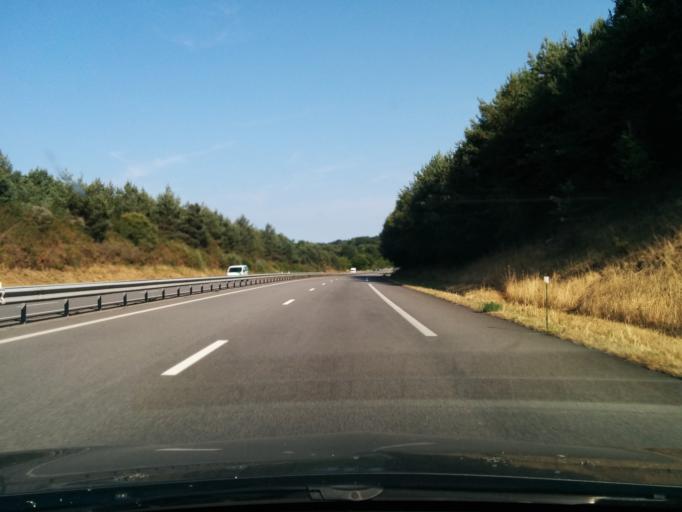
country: FR
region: Limousin
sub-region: Departement de la Haute-Vienne
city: Saint-Germain-les-Belles
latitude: 45.5907
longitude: 1.4627
